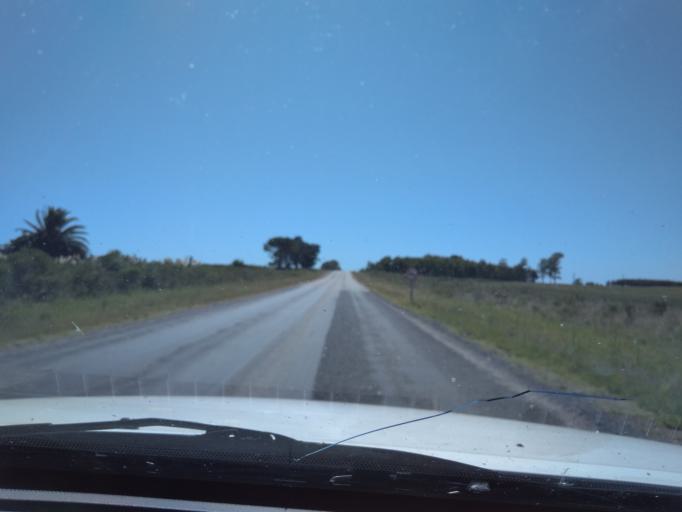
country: UY
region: Florida
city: Florida
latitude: -34.0714
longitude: -56.0683
